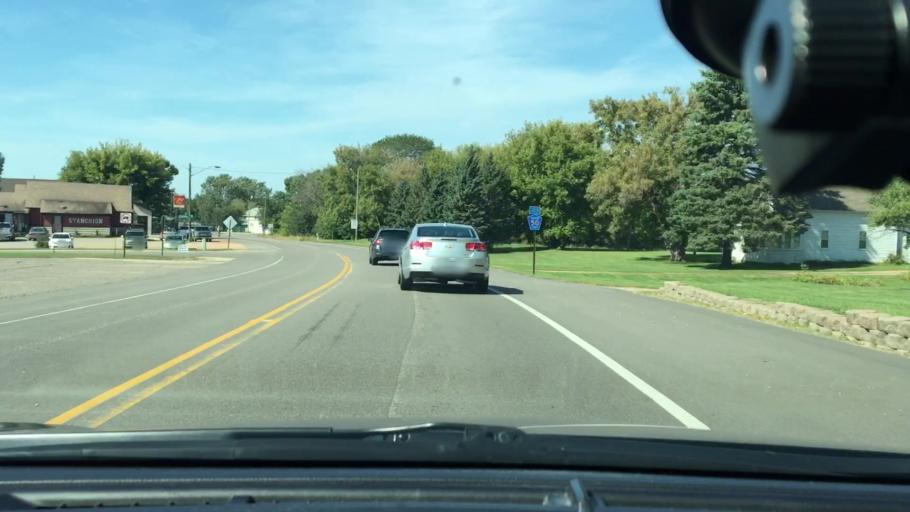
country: US
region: Minnesota
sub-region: Hennepin County
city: Corcoran
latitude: 45.0947
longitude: -93.5451
